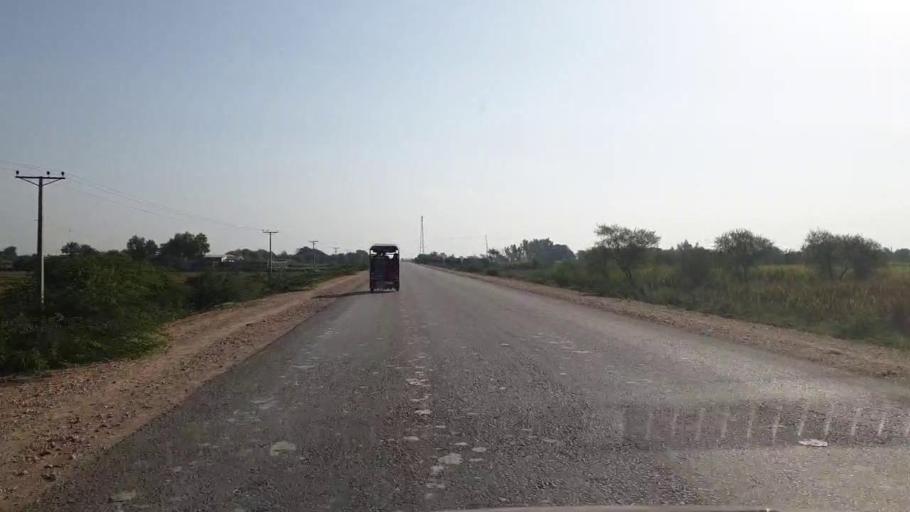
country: PK
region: Sindh
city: Badin
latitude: 24.6586
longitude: 68.9453
